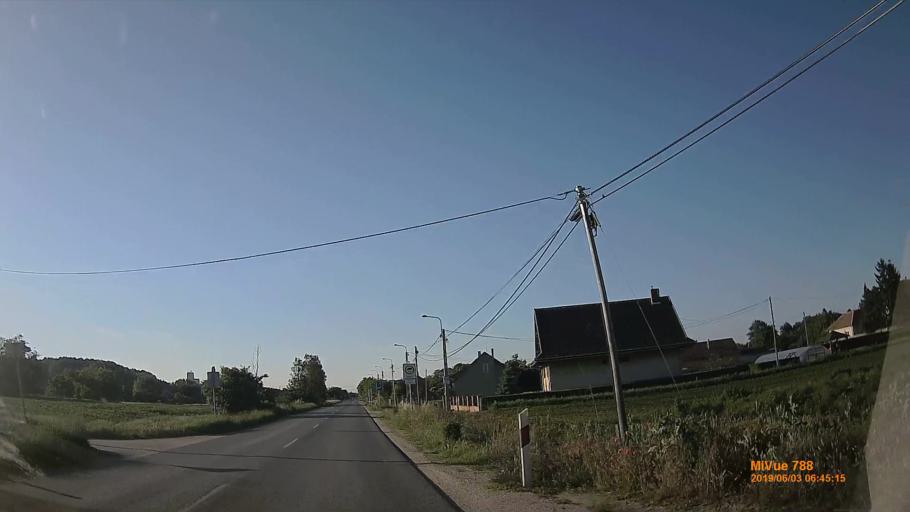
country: HU
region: Pest
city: Bugyi
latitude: 47.2390
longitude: 19.1346
